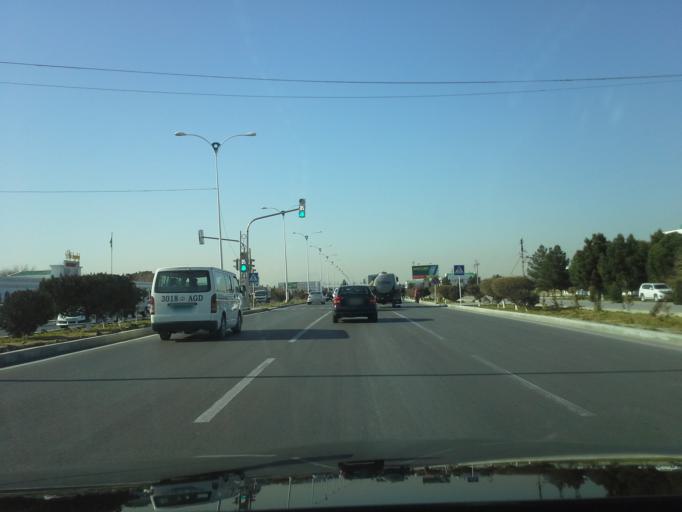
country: TM
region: Ahal
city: Annau
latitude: 37.9080
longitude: 58.5098
